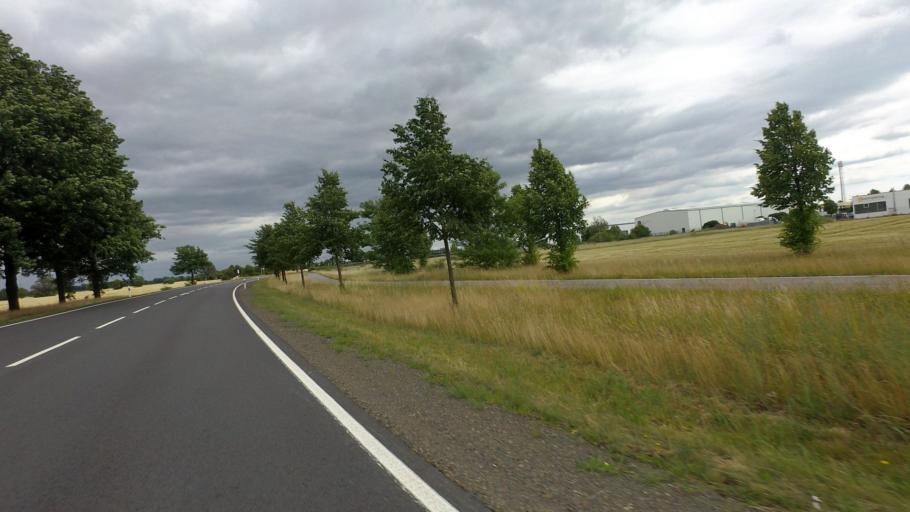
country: DE
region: Saxony
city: Hoyerswerda
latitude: 51.4527
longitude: 14.2176
